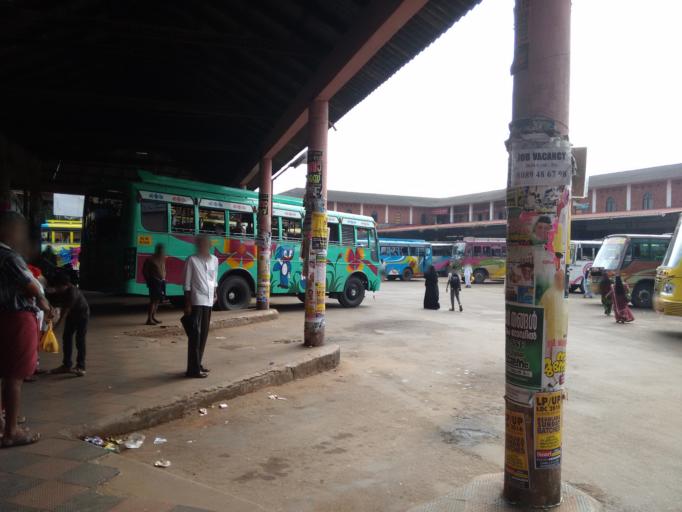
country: IN
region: Kerala
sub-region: Kozhikode
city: Badagara
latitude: 11.5977
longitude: 75.5876
